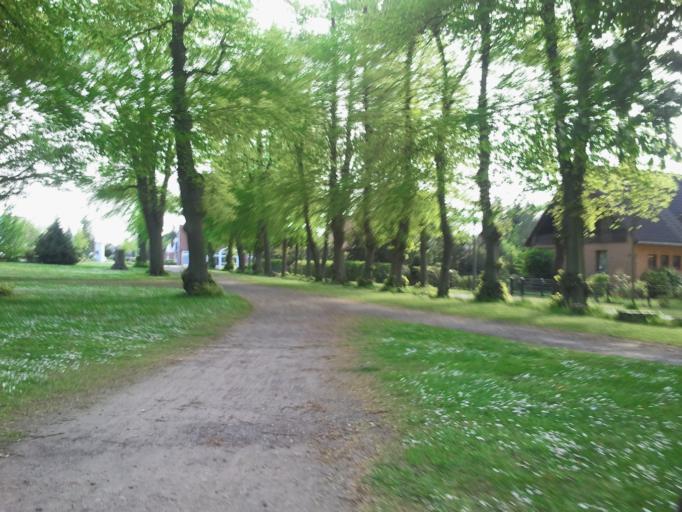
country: DE
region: Lower Saxony
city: Nienburg
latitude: 52.6300
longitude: 9.2217
